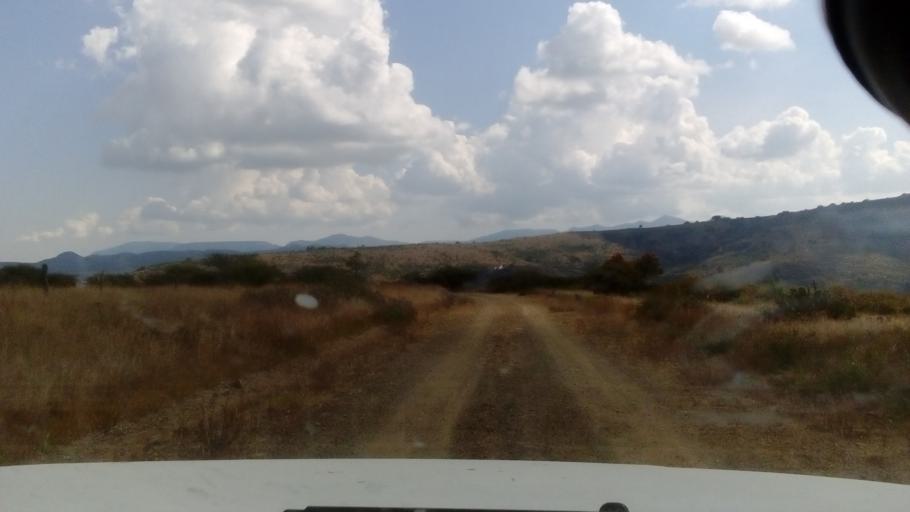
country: MX
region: Guanajuato
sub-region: Leon
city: Lucio Blanco (Los Gavilanes)
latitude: 21.1872
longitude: -101.4711
